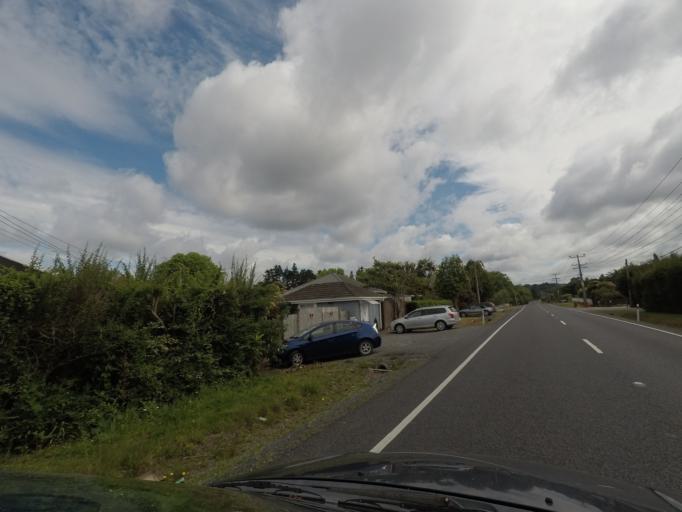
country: NZ
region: Auckland
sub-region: Auckland
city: Muriwai Beach
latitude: -36.7669
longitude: 174.5764
